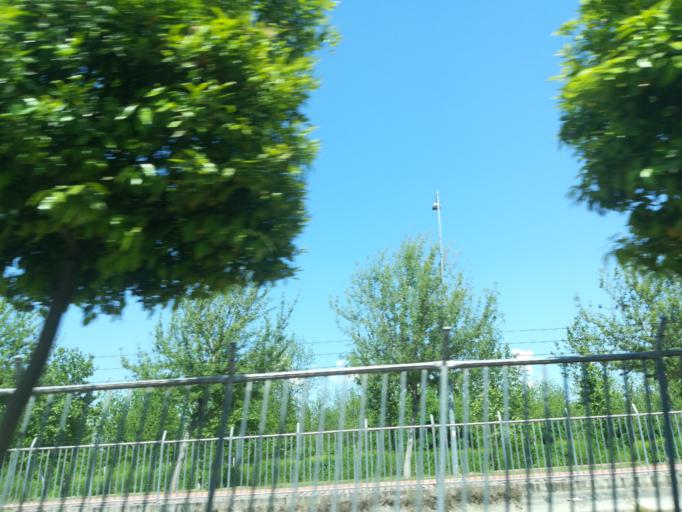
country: TR
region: Adana
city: Adana
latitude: 37.0202
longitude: 35.3724
